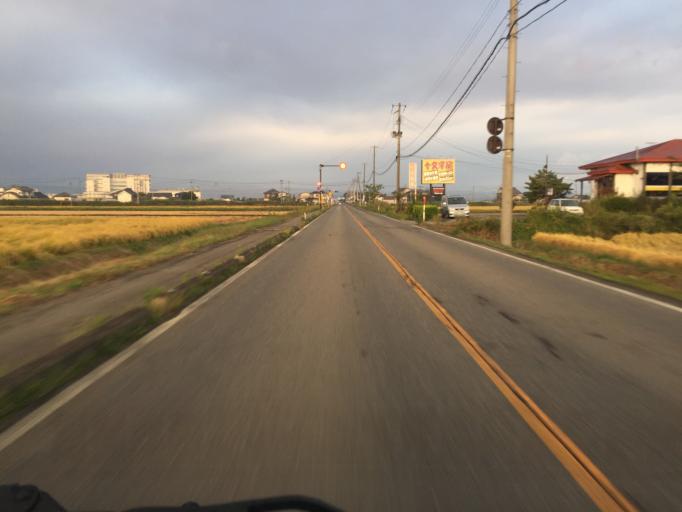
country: JP
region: Fukushima
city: Kitakata
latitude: 37.5543
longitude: 139.9148
